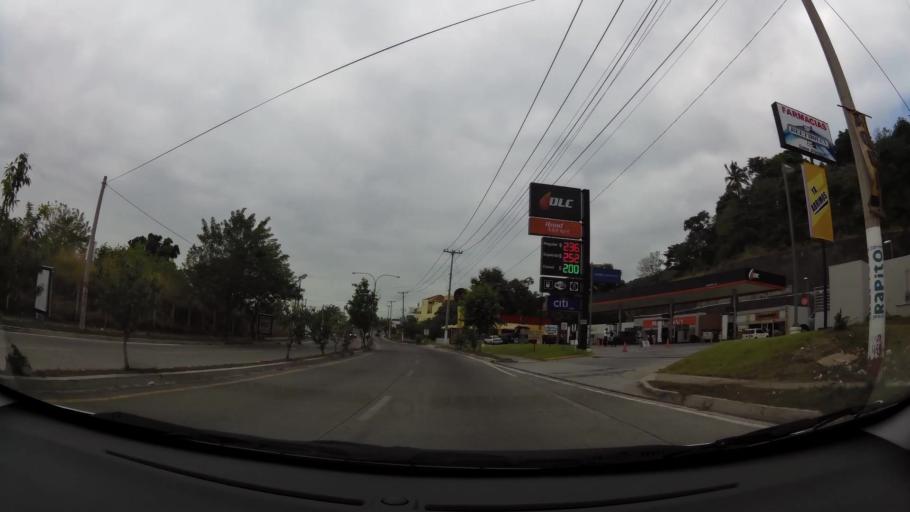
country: SV
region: San Salvador
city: Mejicanos
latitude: 13.7195
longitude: -89.2415
